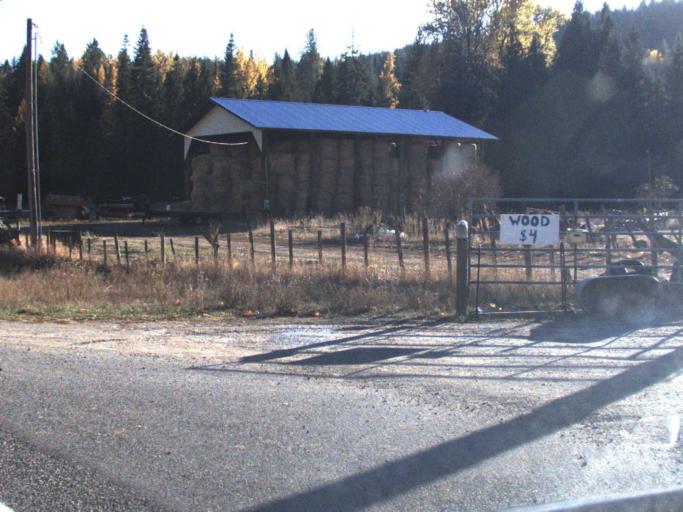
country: CA
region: British Columbia
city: Rossland
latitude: 48.9912
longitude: -117.8297
